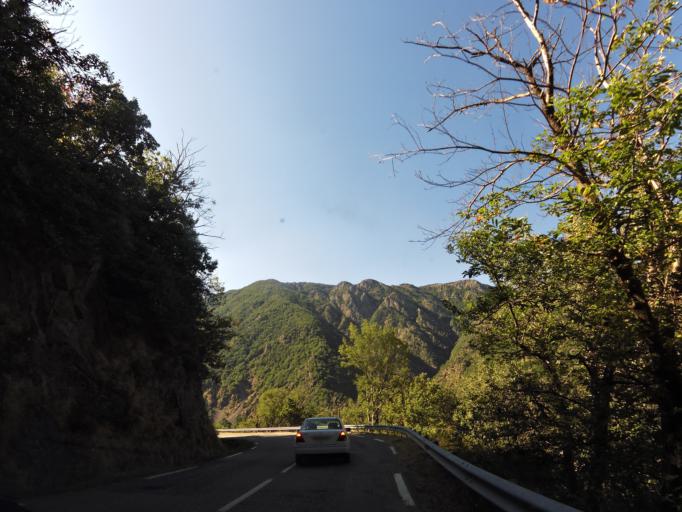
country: FR
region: Languedoc-Roussillon
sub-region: Departement du Gard
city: Valleraugue
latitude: 44.0933
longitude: 3.5740
